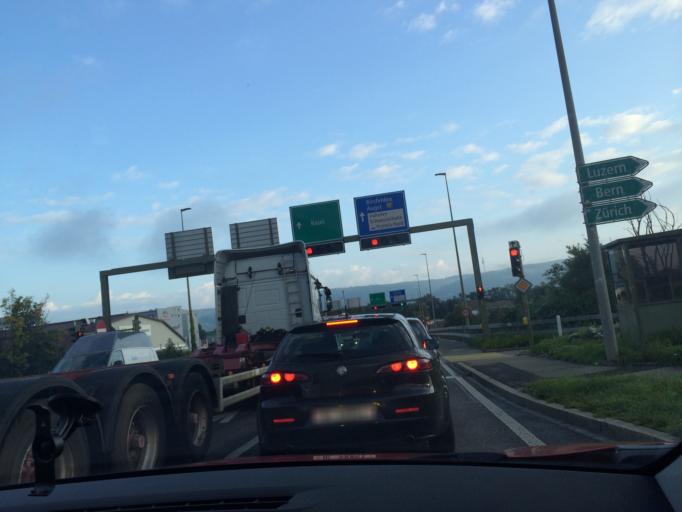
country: CH
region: Basel-Landschaft
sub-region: Bezirk Liestal
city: Pratteln
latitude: 47.5284
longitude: 7.6873
